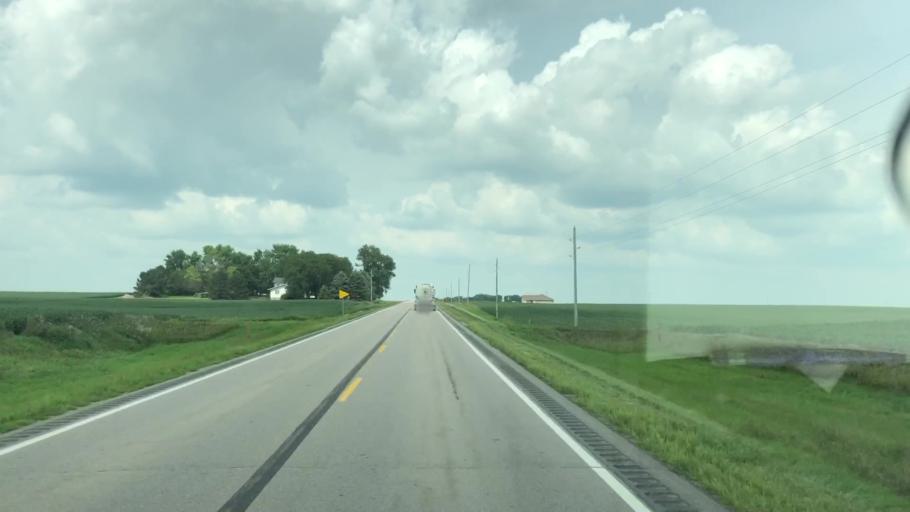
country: US
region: Iowa
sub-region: Plymouth County
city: Remsen
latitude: 42.7884
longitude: -95.9578
